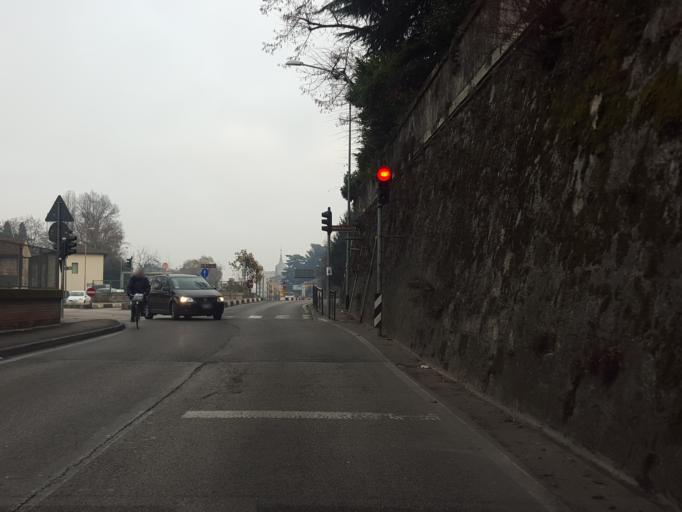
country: IT
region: Veneto
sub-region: Provincia di Vicenza
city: Vicenza
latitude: 45.5409
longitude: 11.5469
